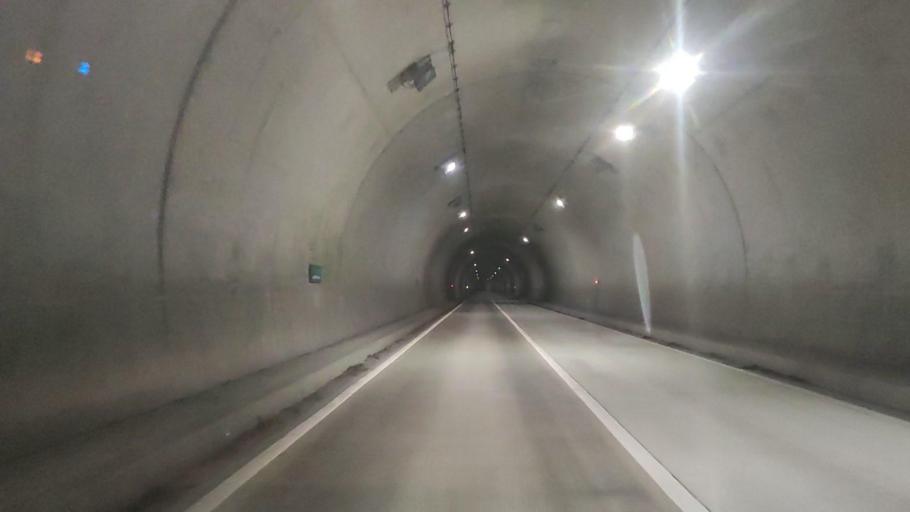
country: JP
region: Kumamoto
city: Matsubase
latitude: 32.4781
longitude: 130.8860
